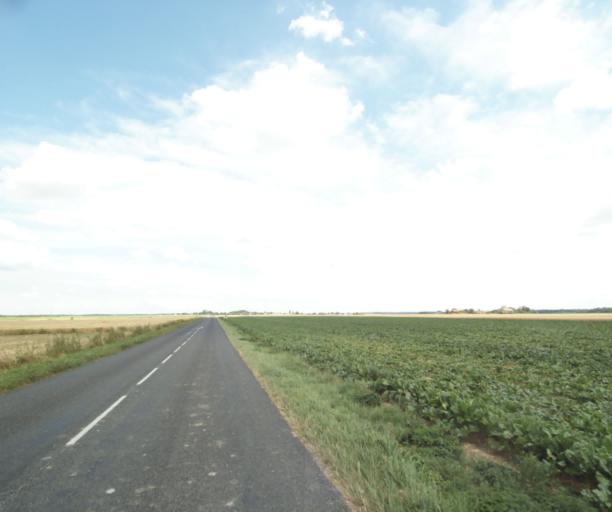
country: FR
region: Ile-de-France
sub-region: Departement de Seine-et-Marne
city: Hericy
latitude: 48.4492
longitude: 2.8044
